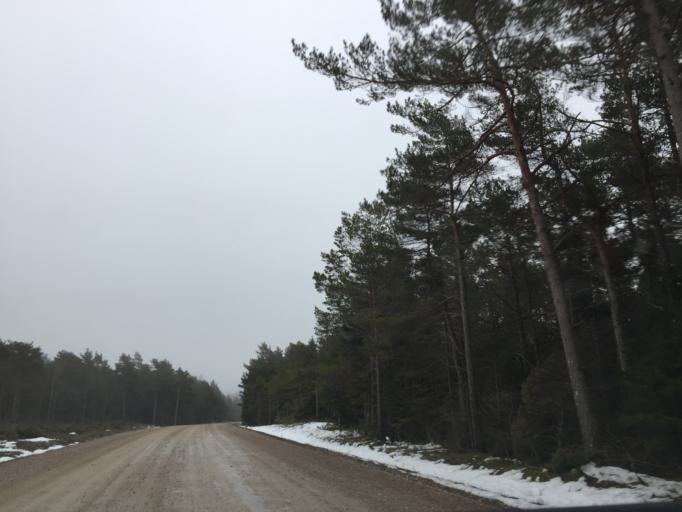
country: EE
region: Saare
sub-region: Kuressaare linn
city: Kuressaare
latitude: 58.4863
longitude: 21.9936
